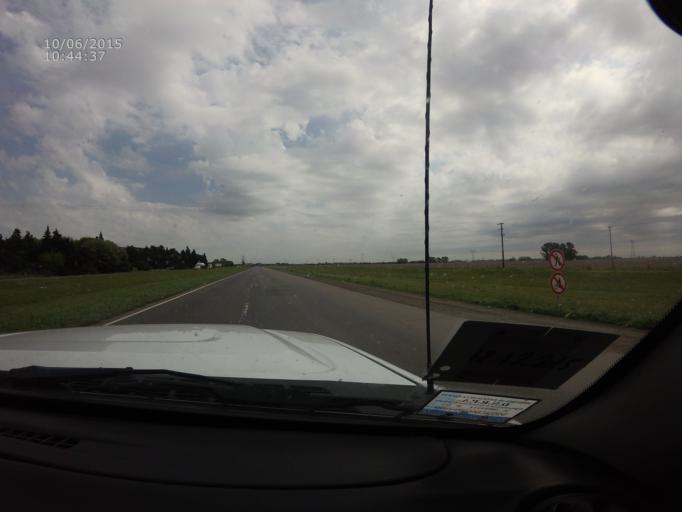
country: AR
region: Buenos Aires
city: San Nicolas de los Arroyos
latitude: -33.4441
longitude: -60.1644
